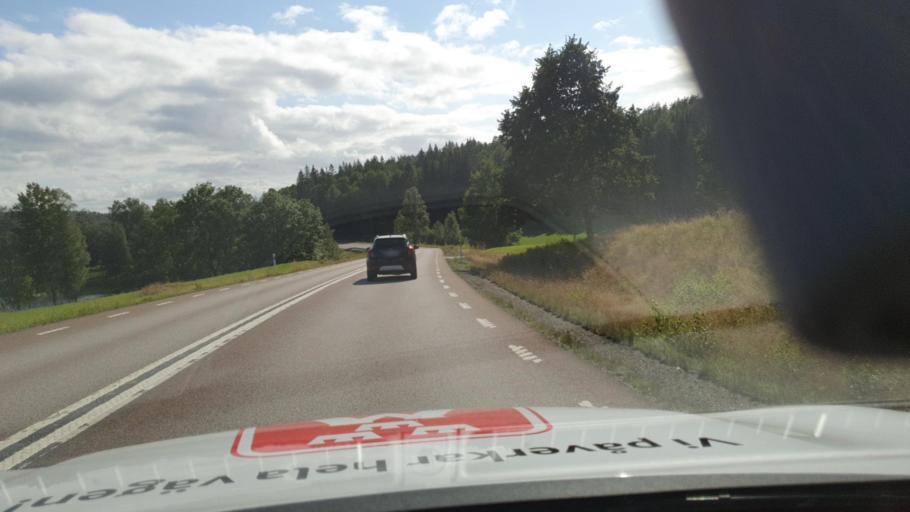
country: SE
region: Vaestra Goetaland
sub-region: Dals-Ed Kommun
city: Ed
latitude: 58.9254
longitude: 12.0343
